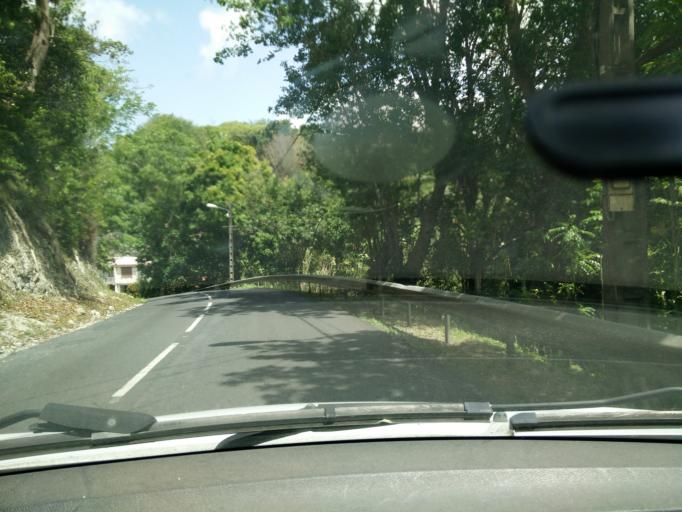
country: GP
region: Guadeloupe
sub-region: Guadeloupe
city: Les Abymes
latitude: 16.2874
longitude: -61.4488
